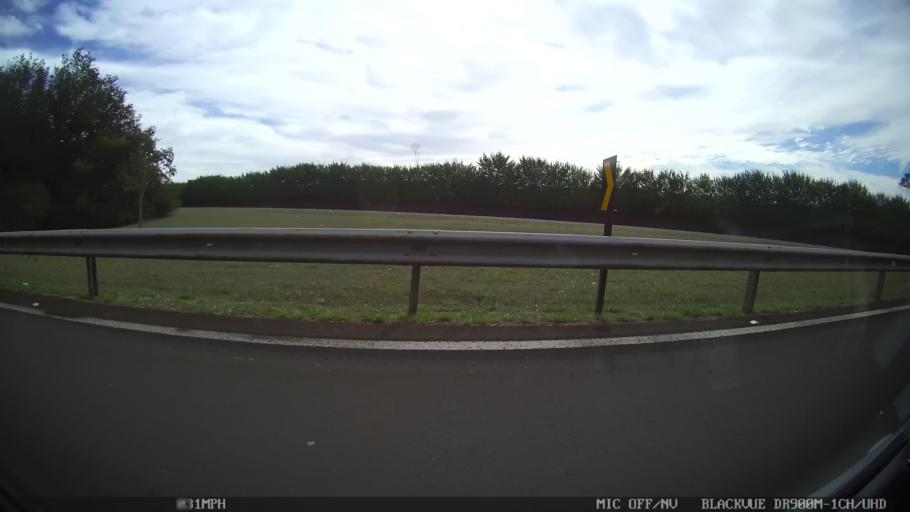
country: BR
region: Sao Paulo
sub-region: Taquaritinga
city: Taquaritinga
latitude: -21.4739
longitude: -48.5985
